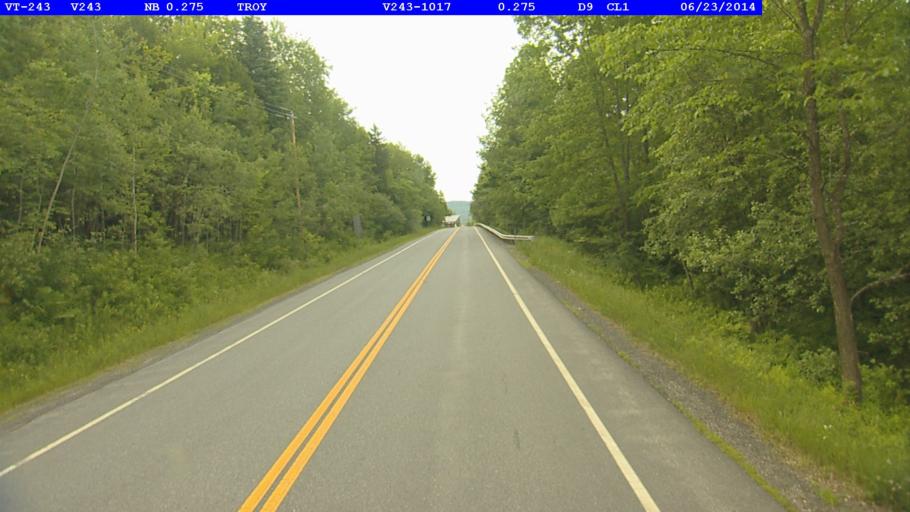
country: US
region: Vermont
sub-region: Orleans County
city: Newport
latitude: 45.0035
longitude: -72.4137
